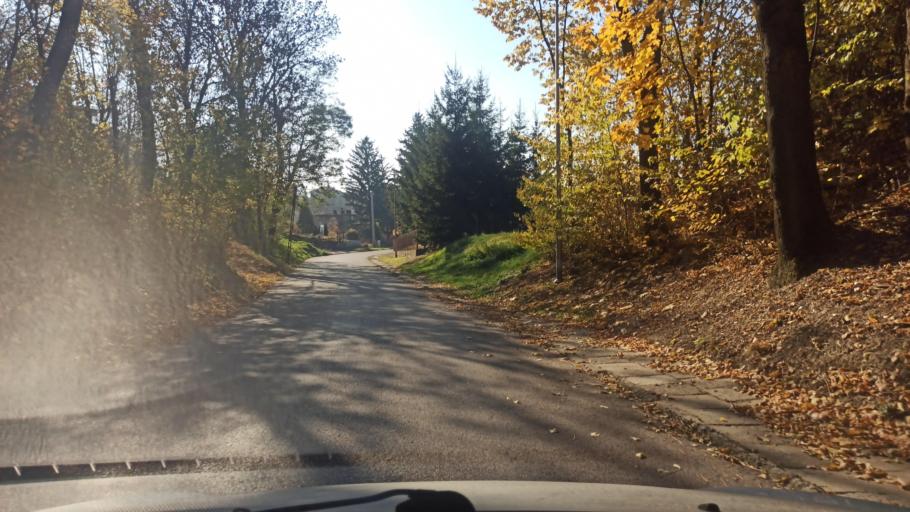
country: PL
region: Subcarpathian Voivodeship
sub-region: Powiat jaroslawski
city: Radymno
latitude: 49.9460
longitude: 22.8224
